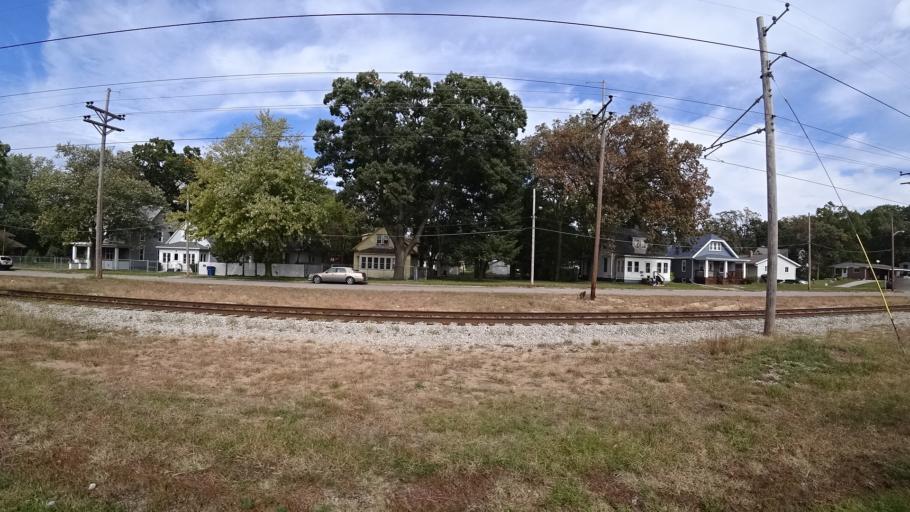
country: US
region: Indiana
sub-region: LaPorte County
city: Michigan City
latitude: 41.7131
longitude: -86.8827
